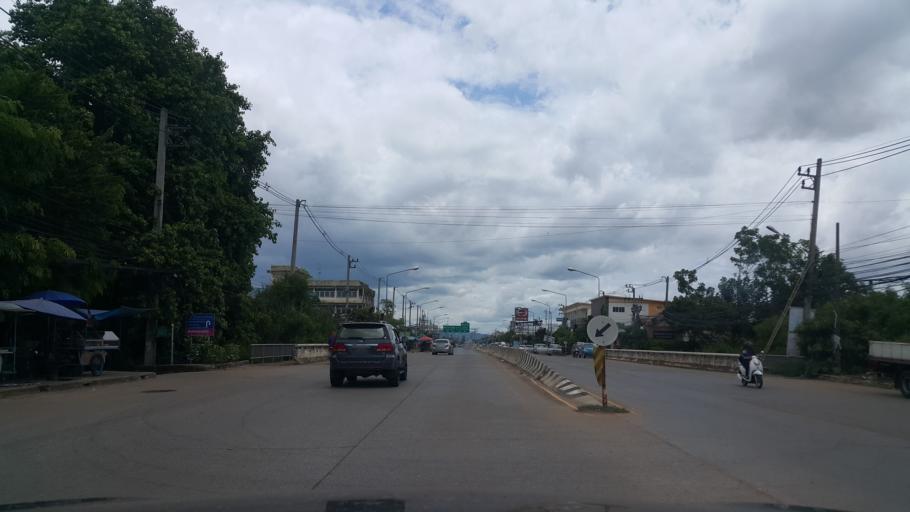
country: TH
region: Sukhothai
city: Sukhothai
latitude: 17.0088
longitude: 99.8100
